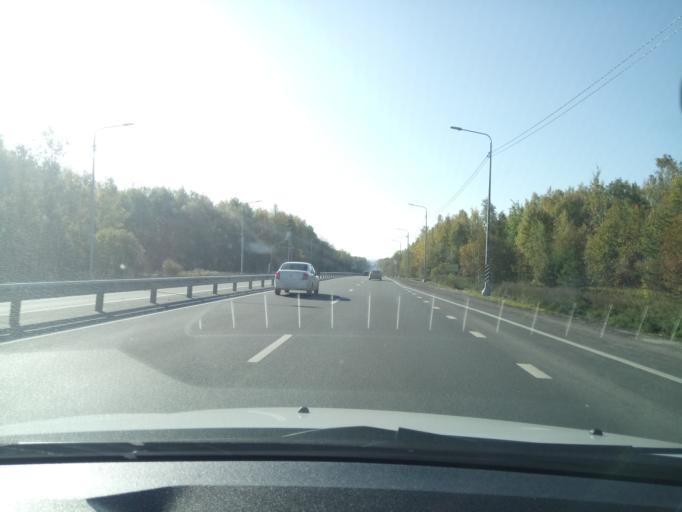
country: RU
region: Nizjnij Novgorod
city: Burevestnik
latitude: 56.0330
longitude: 43.9616
